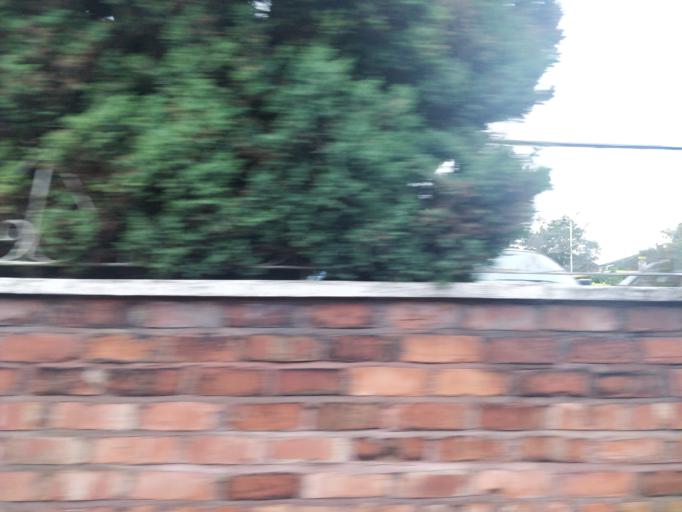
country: GB
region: England
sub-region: Sefton
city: Southport
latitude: 53.6605
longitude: -2.9703
